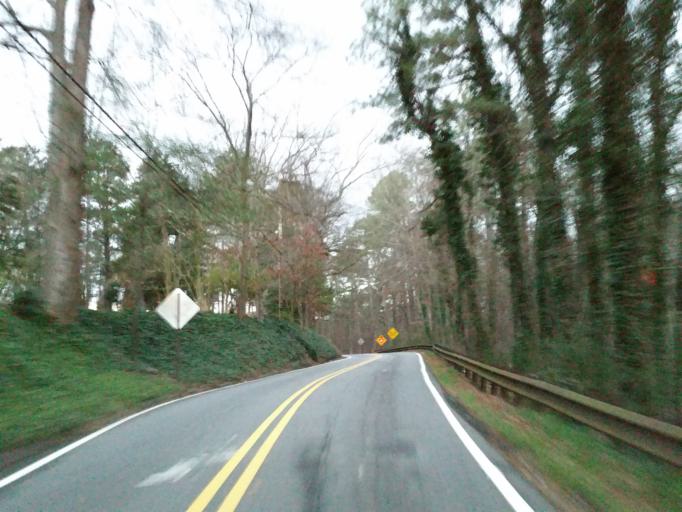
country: US
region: Georgia
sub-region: Cobb County
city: Mableton
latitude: 33.8500
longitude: -84.5585
